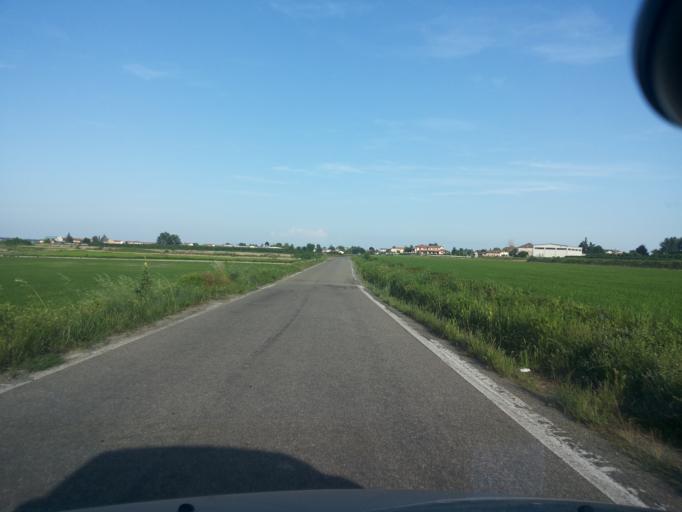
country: IT
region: Piedmont
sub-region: Provincia di Vercelli
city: Pezzana
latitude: 45.2676
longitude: 8.4732
